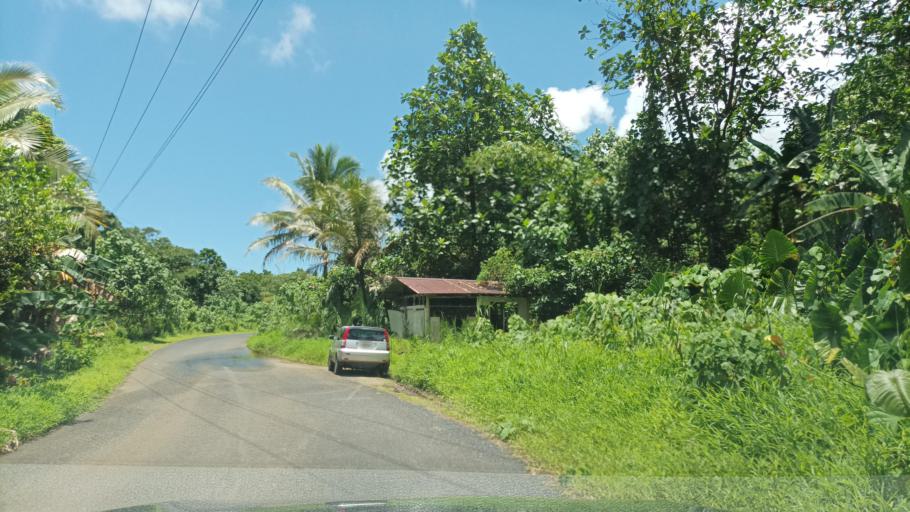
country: FM
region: Pohnpei
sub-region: Madolenihm Municipality
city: Madolenihm Municipality Government
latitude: 6.8693
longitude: 158.2872
